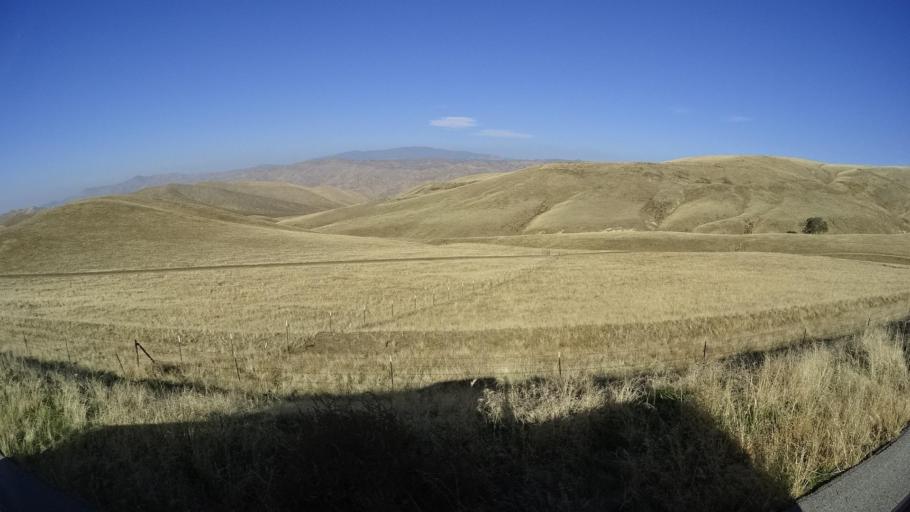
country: US
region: California
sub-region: Kern County
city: Bear Valley Springs
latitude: 35.2711
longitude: -118.6844
